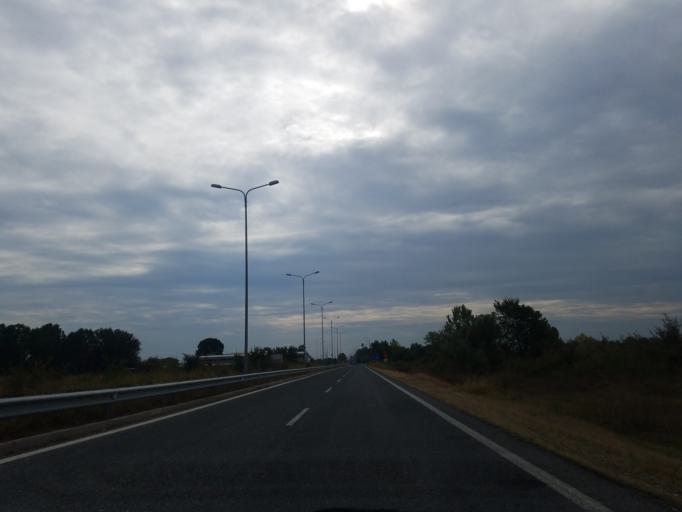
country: GR
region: Thessaly
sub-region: Trikala
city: Pyrgetos
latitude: 39.5321
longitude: 21.7417
